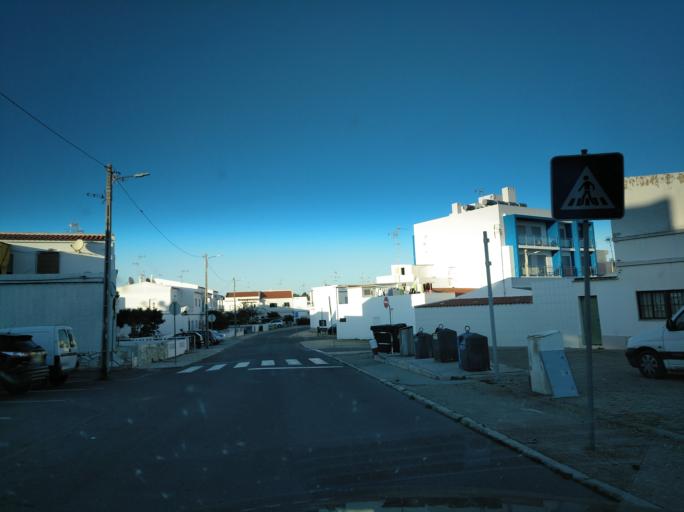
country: PT
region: Faro
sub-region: Vila Real de Santo Antonio
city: Monte Gordo
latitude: 37.1801
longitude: -7.4576
